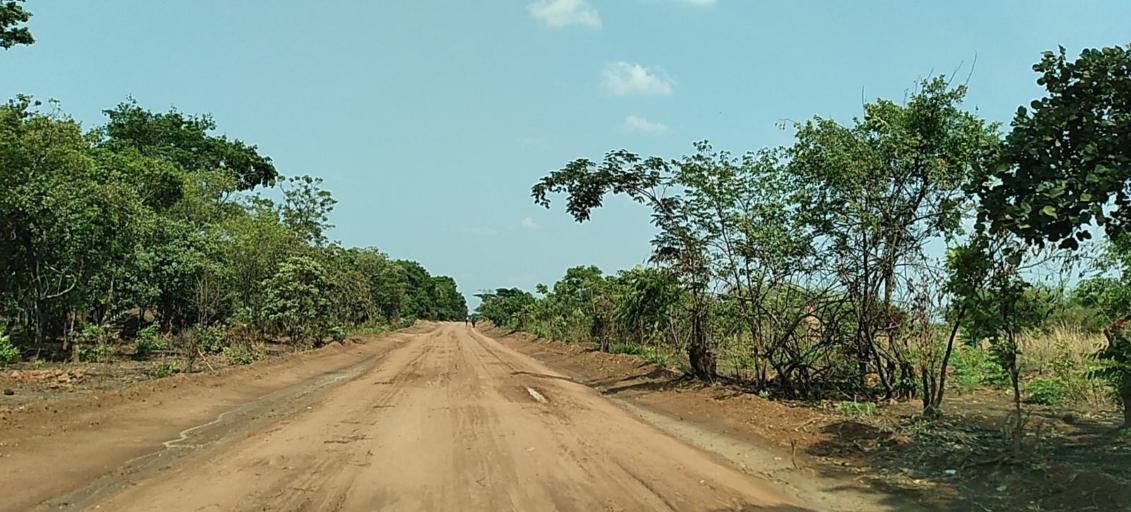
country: ZM
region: Copperbelt
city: Luanshya
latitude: -13.0907
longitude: 28.2823
